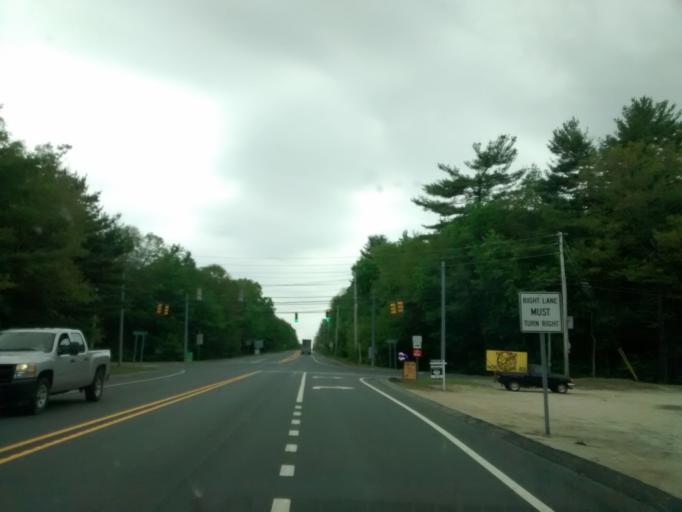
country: US
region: Rhode Island
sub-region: Providence County
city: Harrisville
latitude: 41.9560
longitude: -71.6524
